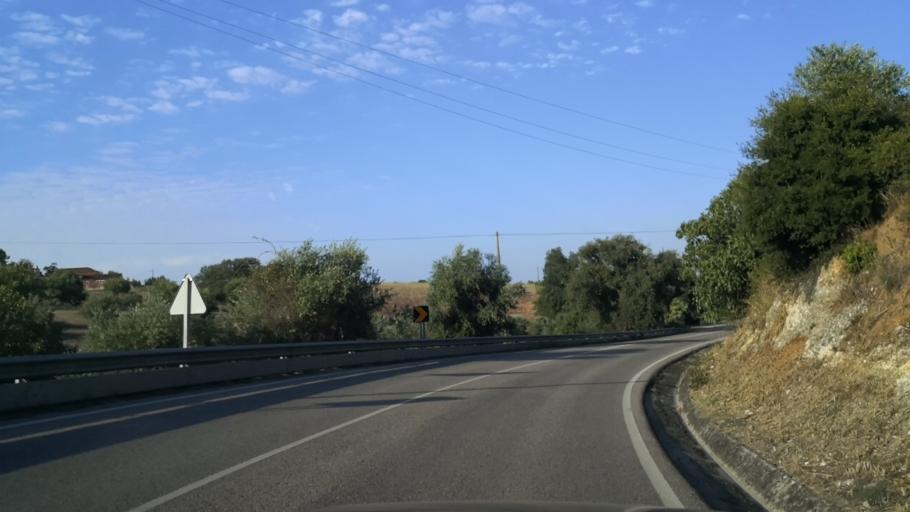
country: PT
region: Santarem
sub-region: Alcanena
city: Alcanena
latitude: 39.3551
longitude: -8.6640
